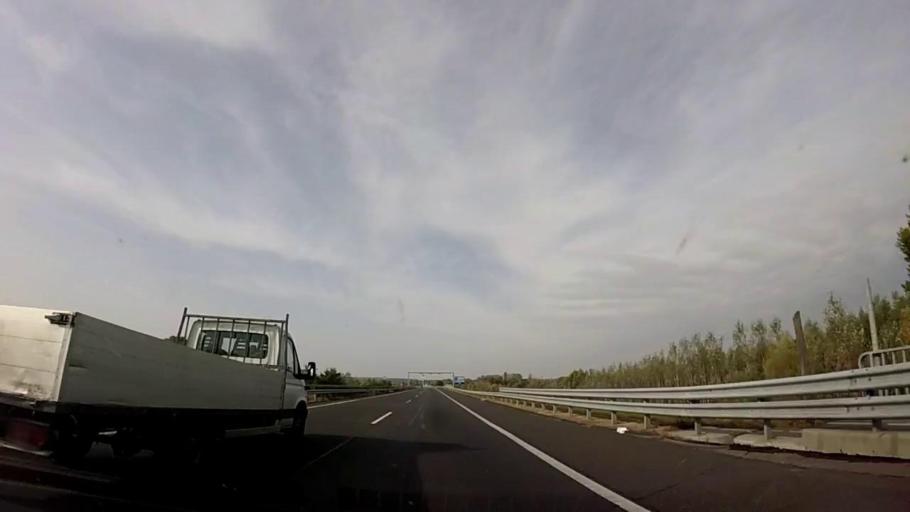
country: HU
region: Somogy
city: Kethely
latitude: 46.6855
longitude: 17.3893
